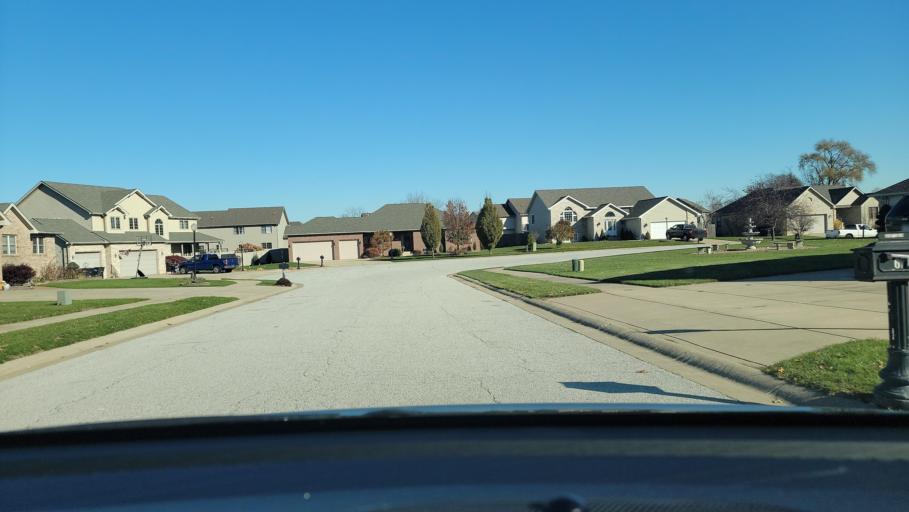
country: US
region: Indiana
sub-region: Porter County
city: Portage
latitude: 41.5882
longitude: -87.1520
